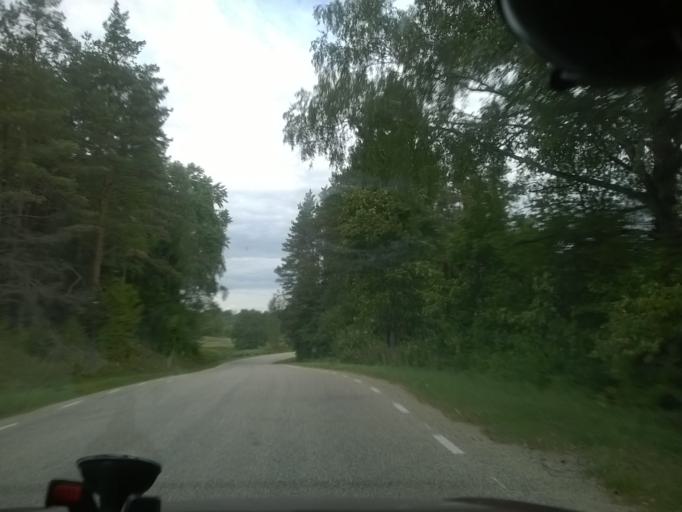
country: EE
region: Vorumaa
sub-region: Voru linn
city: Voru
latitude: 57.7751
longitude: 27.0257
